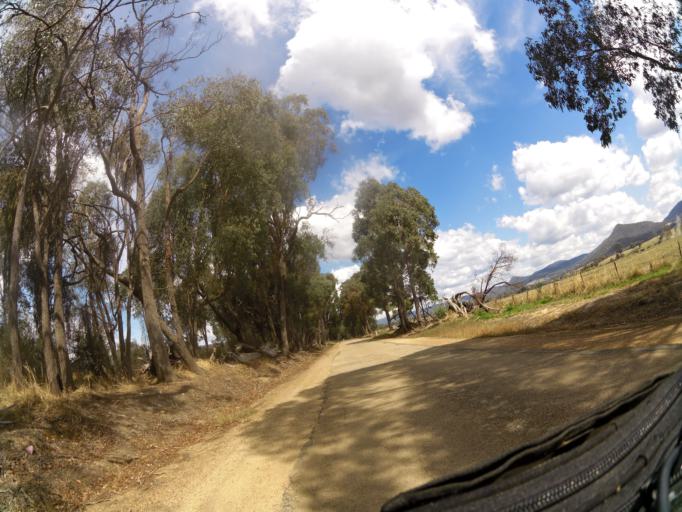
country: AU
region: Victoria
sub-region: Benalla
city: Benalla
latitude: -36.7656
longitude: 145.9762
